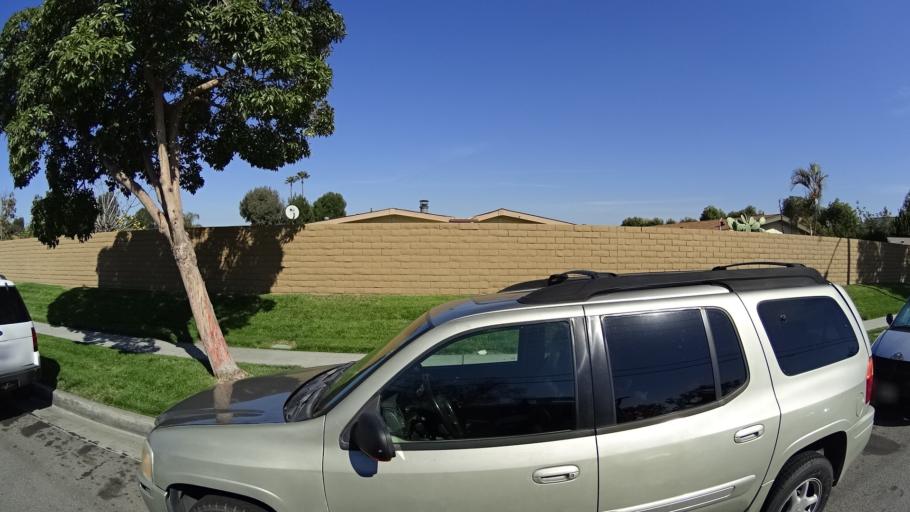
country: US
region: California
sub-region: Orange County
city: Fullerton
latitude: 33.8518
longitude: -117.9457
